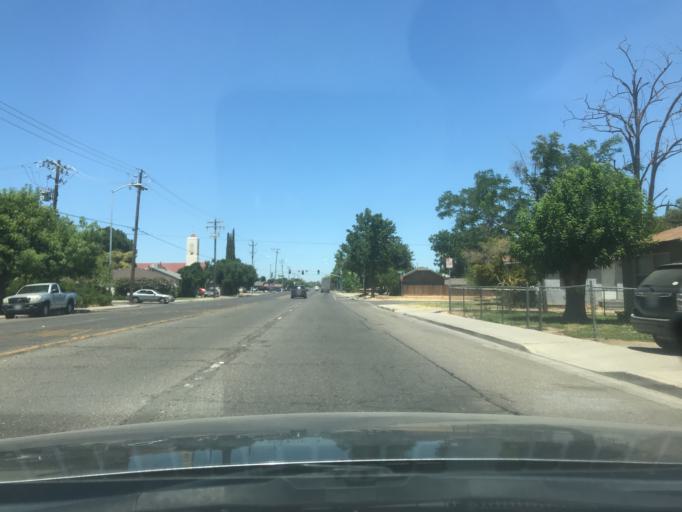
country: US
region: California
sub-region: Merced County
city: Atwater
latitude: 37.3539
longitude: -120.6137
